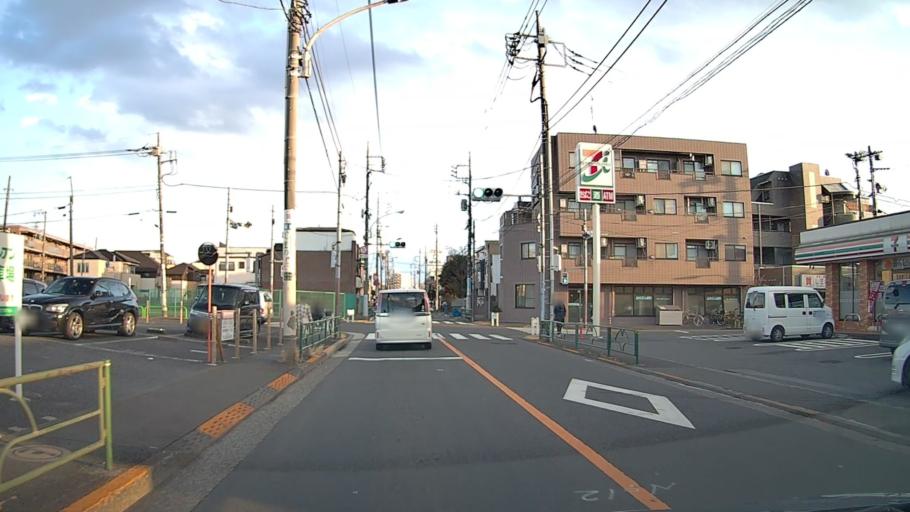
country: JP
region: Saitama
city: Wako
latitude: 35.7533
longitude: 139.6605
